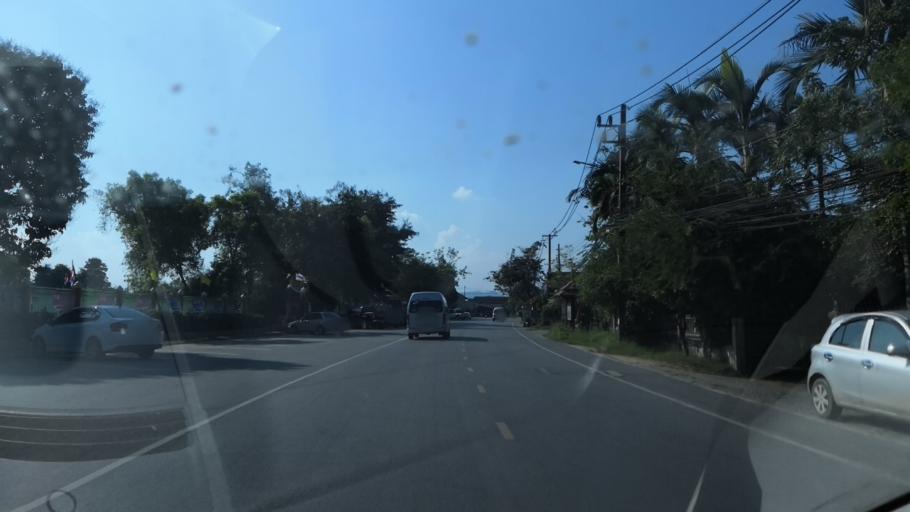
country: TH
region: Chiang Rai
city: Chiang Rai
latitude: 19.9287
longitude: 99.8528
